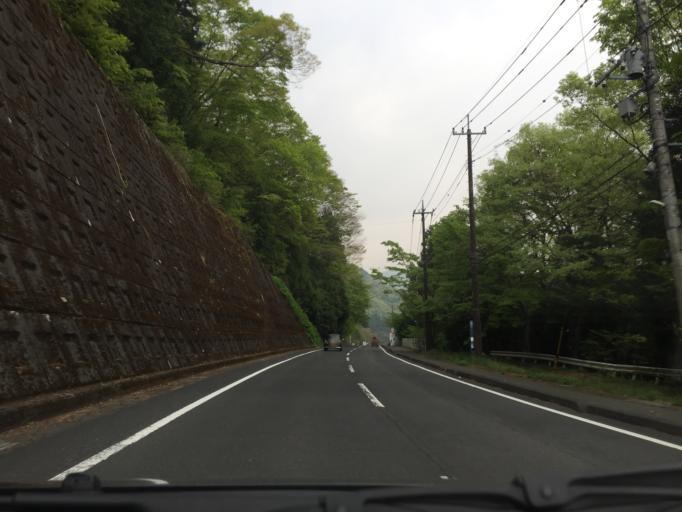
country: JP
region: Tochigi
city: Imaichi
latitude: 36.8432
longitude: 139.7205
